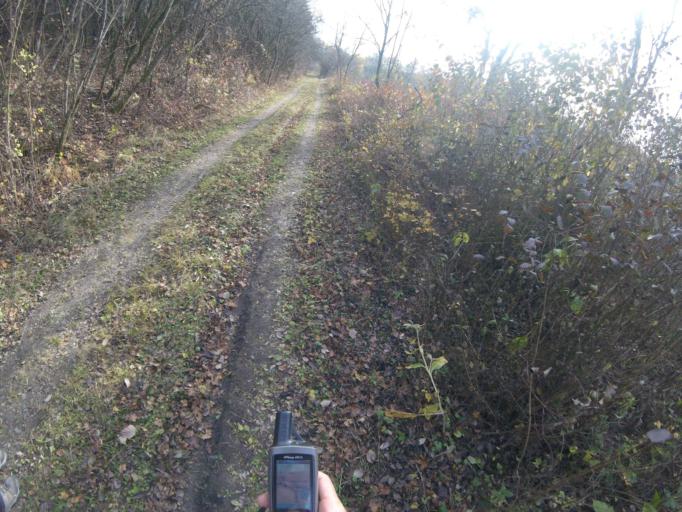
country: HU
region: Borsod-Abauj-Zemplen
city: Gonc
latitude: 48.5009
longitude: 21.4520
